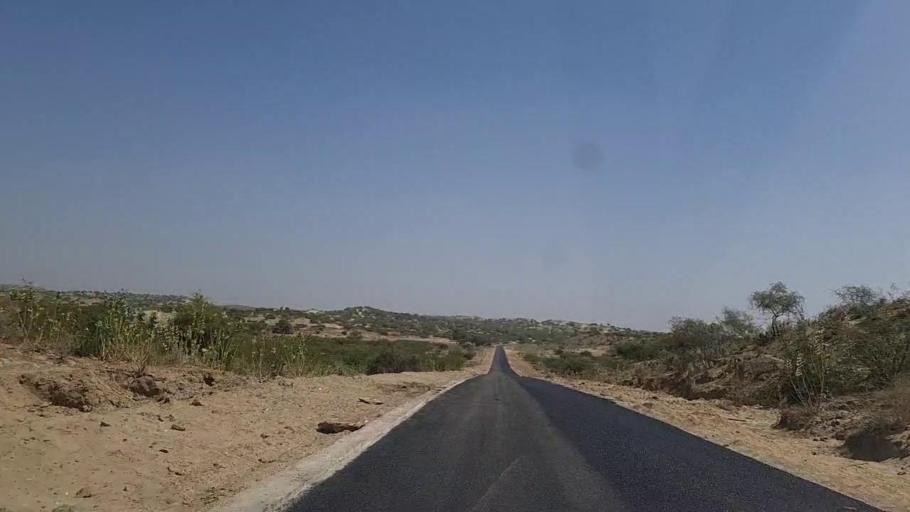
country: PK
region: Sindh
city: Diplo
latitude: 24.4800
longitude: 69.5170
